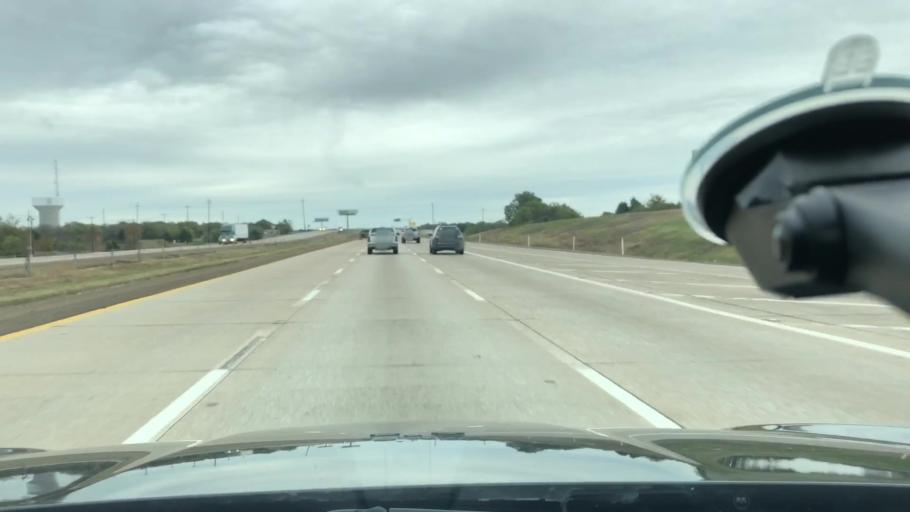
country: US
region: Texas
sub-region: Dallas County
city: Balch Springs
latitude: 32.7043
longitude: -96.5816
